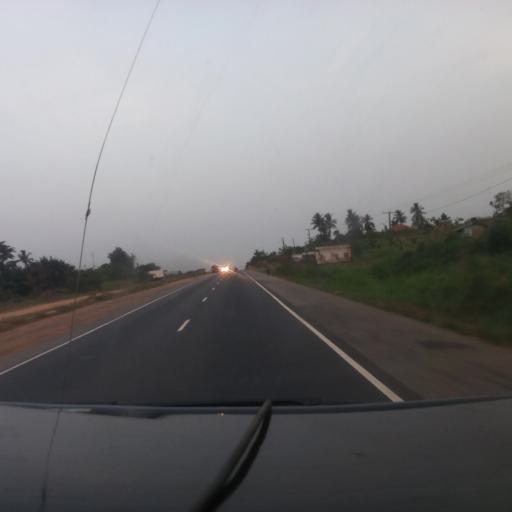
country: GH
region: Eastern
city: Nsawam
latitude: 5.8804
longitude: -0.3744
